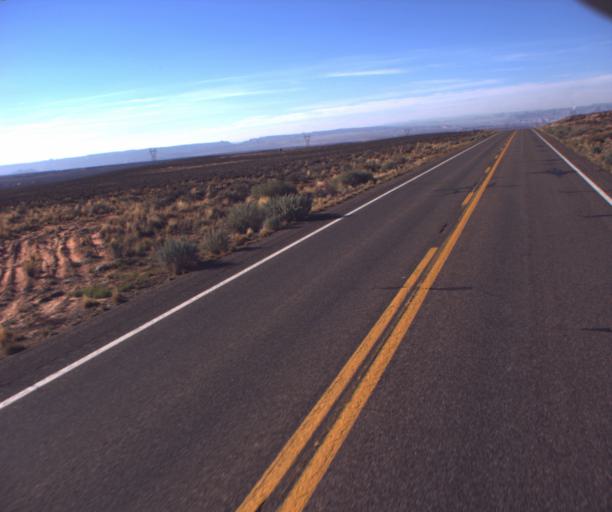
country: US
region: Arizona
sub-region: Coconino County
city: LeChee
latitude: 36.8297
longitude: -111.3122
